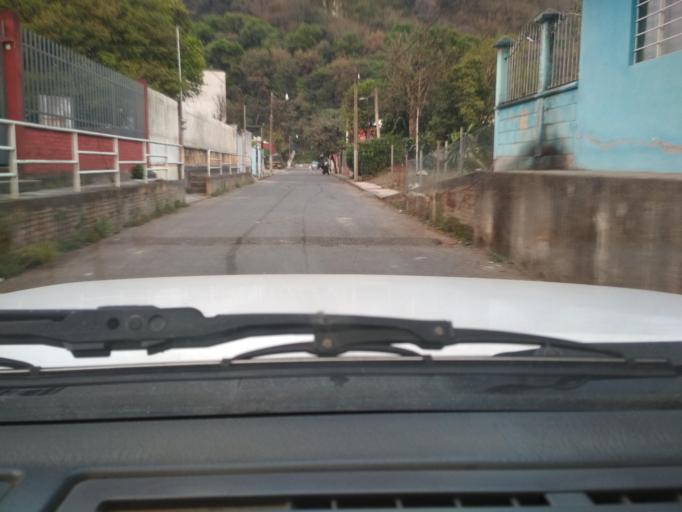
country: MX
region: Veracruz
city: Orizaba
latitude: 18.8596
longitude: -97.0917
